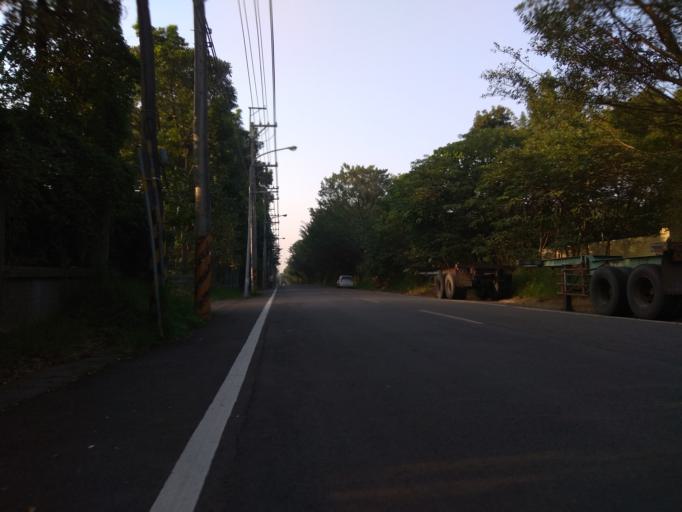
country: TW
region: Taiwan
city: Daxi
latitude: 24.9261
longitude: 121.1817
